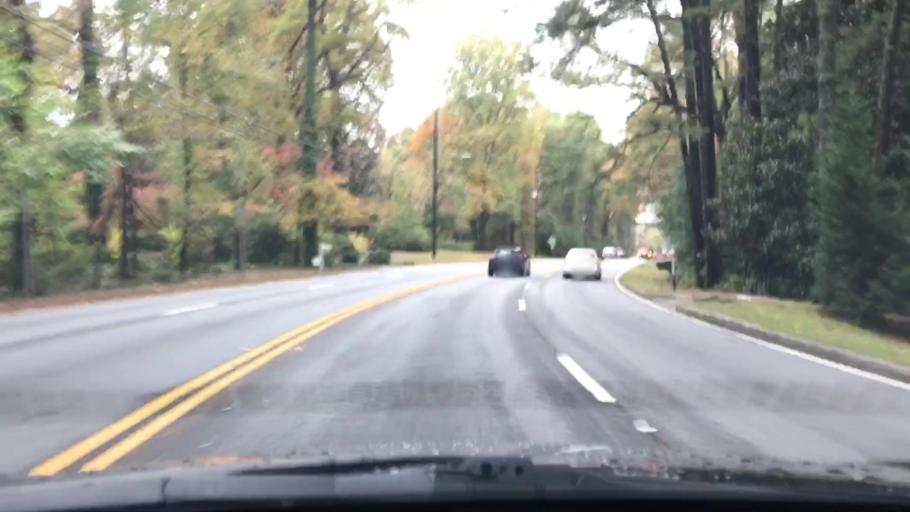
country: US
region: Georgia
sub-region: DeKalb County
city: North Druid Hills
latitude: 33.8220
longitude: -84.3059
